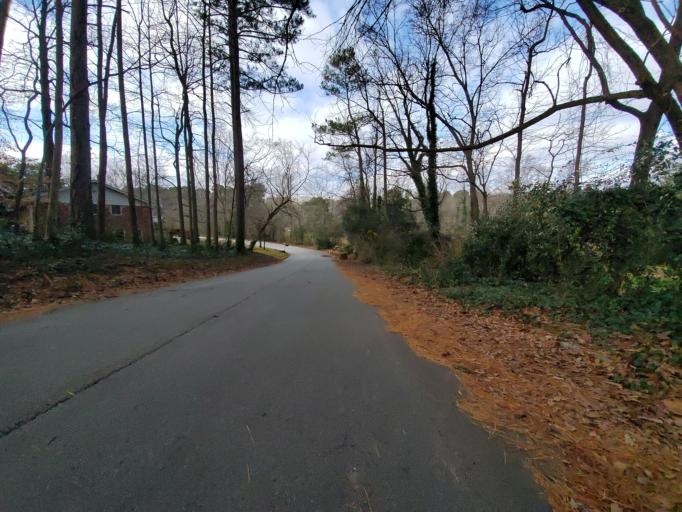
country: US
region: Georgia
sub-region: DeKalb County
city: North Decatur
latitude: 33.8041
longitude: -84.2897
